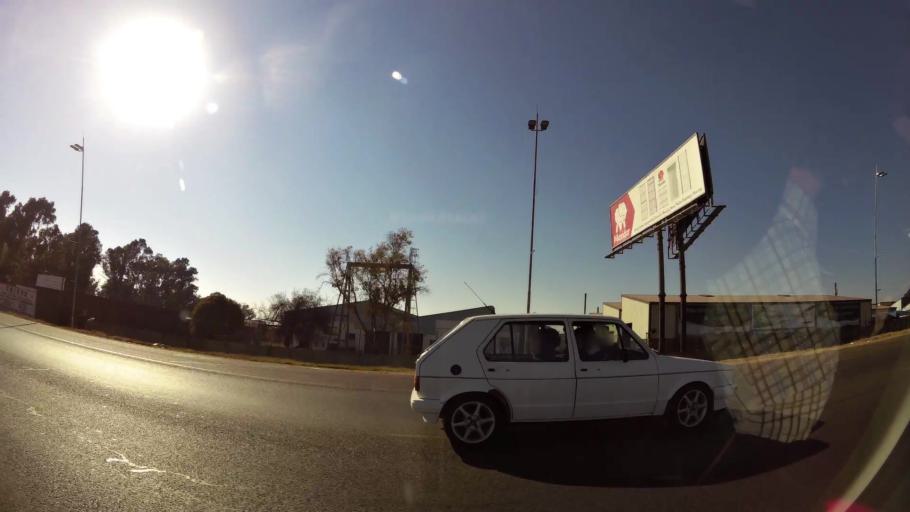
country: ZA
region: Gauteng
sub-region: City of Johannesburg Metropolitan Municipality
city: Modderfontein
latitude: -26.0661
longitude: 28.1859
